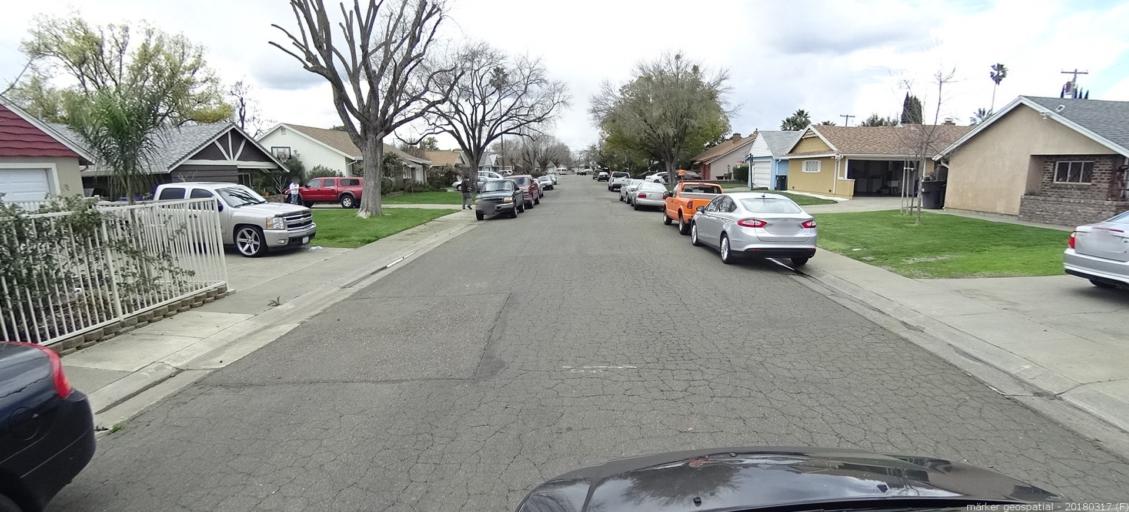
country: US
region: California
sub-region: Sacramento County
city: Parkway
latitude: 38.5007
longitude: -121.4541
